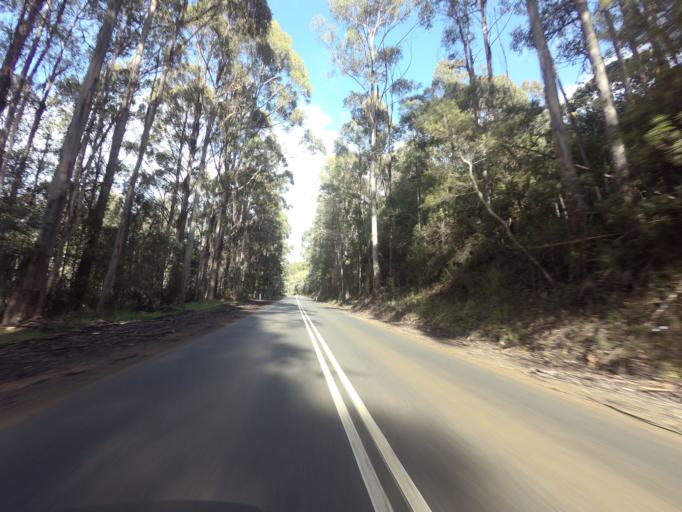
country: AU
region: Tasmania
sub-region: Huon Valley
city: Geeveston
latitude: -43.3427
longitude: 146.9642
